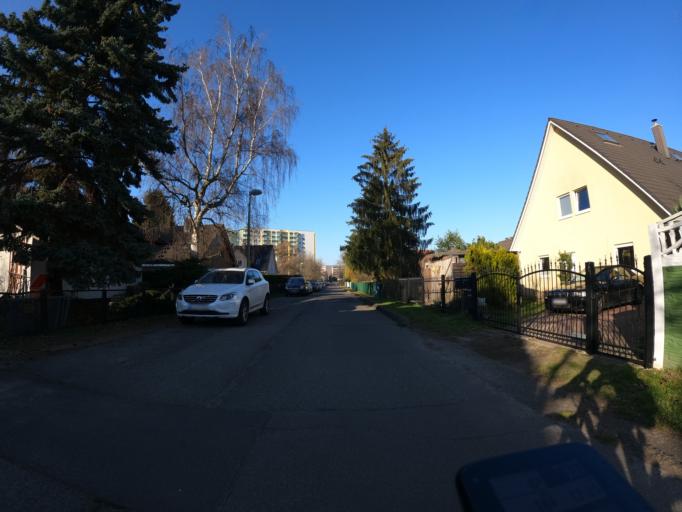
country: DE
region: Berlin
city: Marzahn
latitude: 52.5357
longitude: 13.5552
